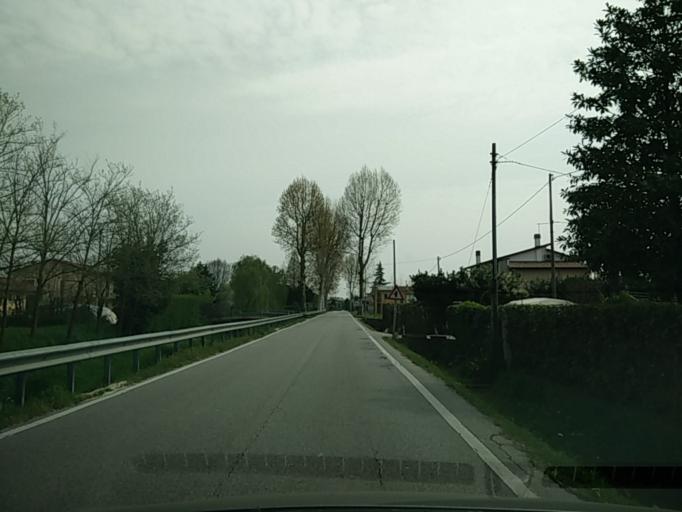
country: IT
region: Veneto
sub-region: Provincia di Venezia
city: Scaltenigo
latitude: 45.4732
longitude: 12.0618
